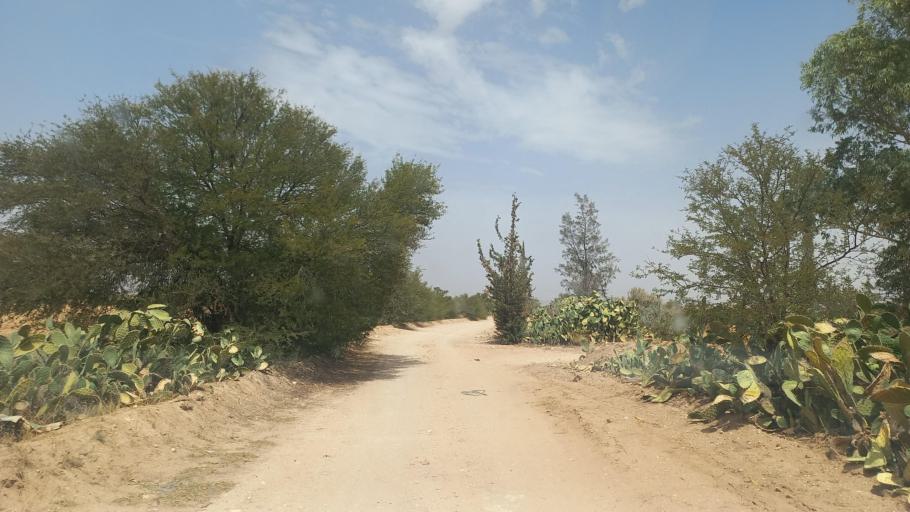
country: TN
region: Al Qasrayn
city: Kasserine
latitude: 35.2522
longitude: 9.0084
